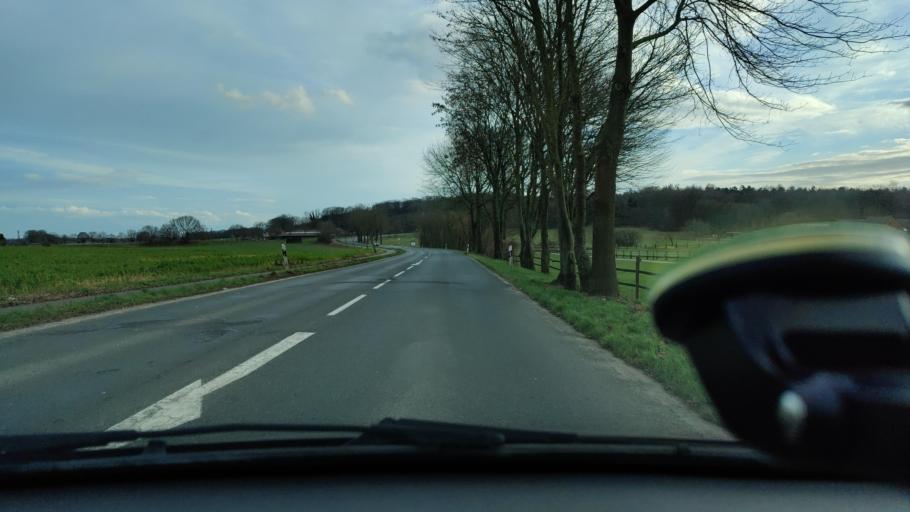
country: DE
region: North Rhine-Westphalia
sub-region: Regierungsbezirk Dusseldorf
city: Xanten
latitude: 51.6422
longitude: 6.4590
